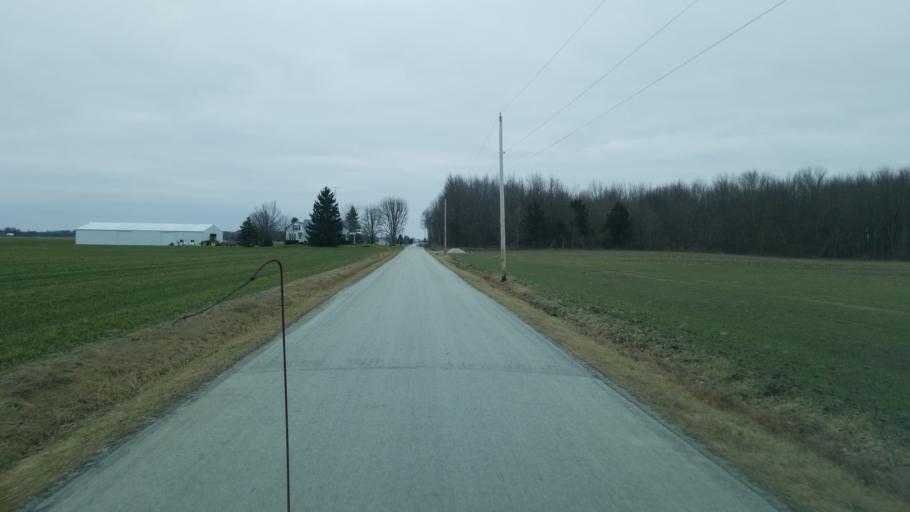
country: US
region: Ohio
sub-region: Hardin County
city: Kenton
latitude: 40.6718
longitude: -83.4957
